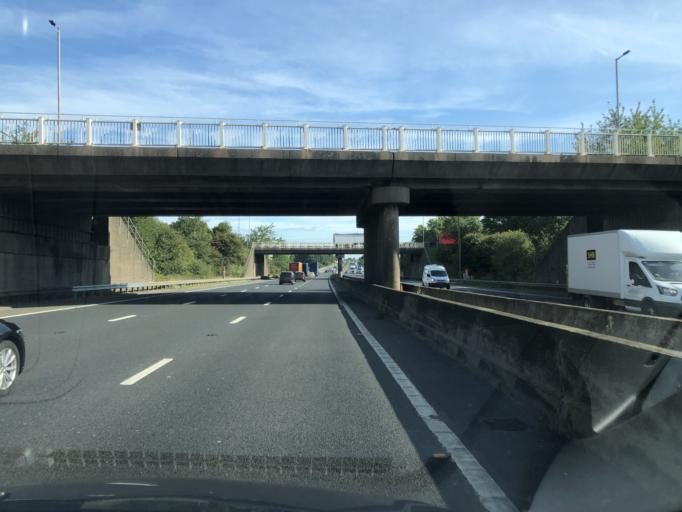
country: GB
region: England
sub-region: Rotherham
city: Hellaby
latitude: 53.4231
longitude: -1.2515
